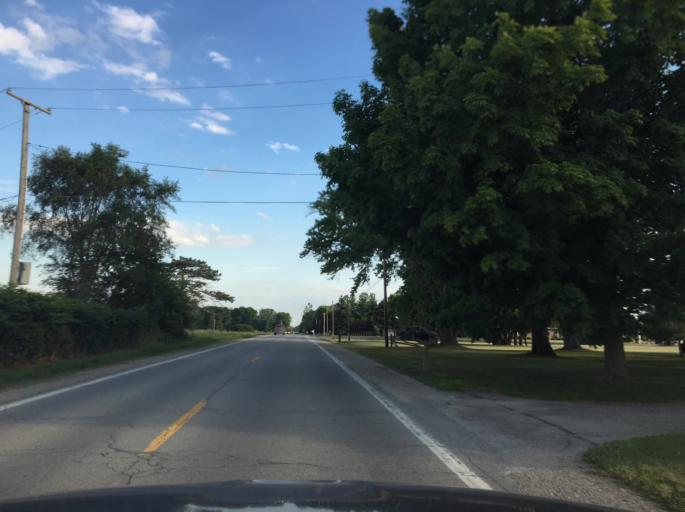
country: US
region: Michigan
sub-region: Macomb County
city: Romeo
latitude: 42.7721
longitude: -82.9614
